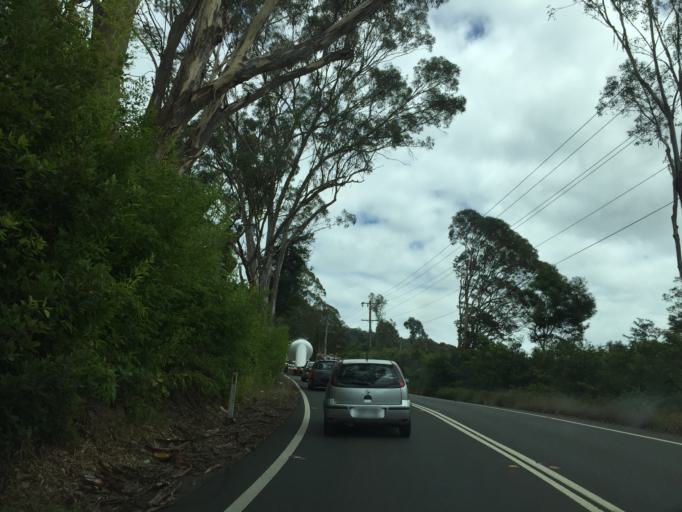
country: AU
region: New South Wales
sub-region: Hawkesbury
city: Richmond
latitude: -33.5448
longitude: 150.6480
